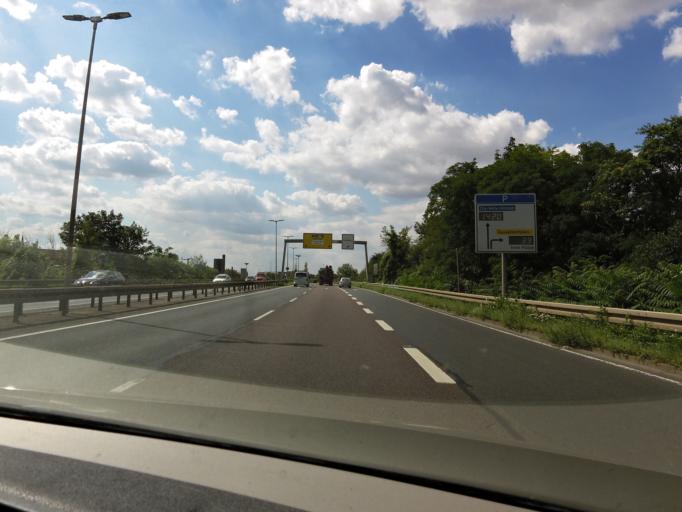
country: DE
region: Saxony-Anhalt
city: Magdeburg
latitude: 52.1206
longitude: 11.6159
